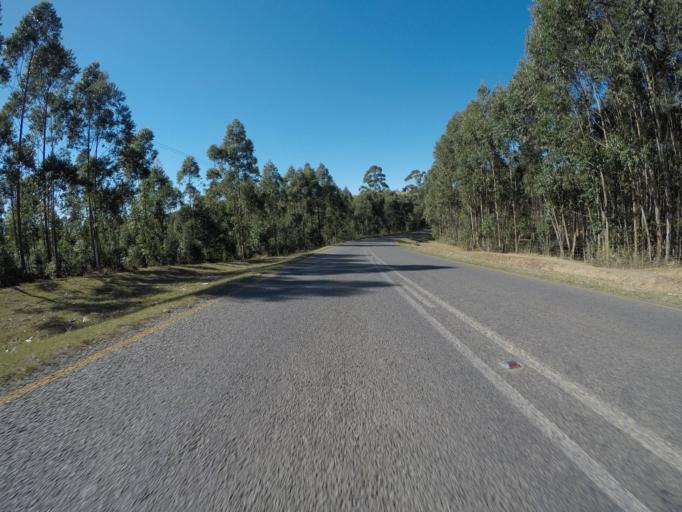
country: ZA
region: Eastern Cape
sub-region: OR Tambo District Municipality
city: Mthatha
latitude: -31.7751
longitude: 28.7376
